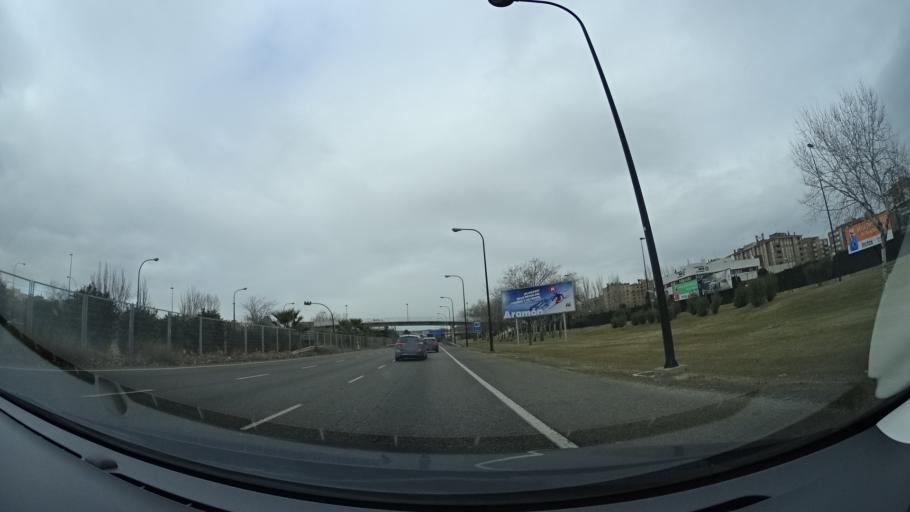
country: ES
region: Aragon
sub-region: Provincia de Zaragoza
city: Zaragoza
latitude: 41.6697
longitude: -0.8800
